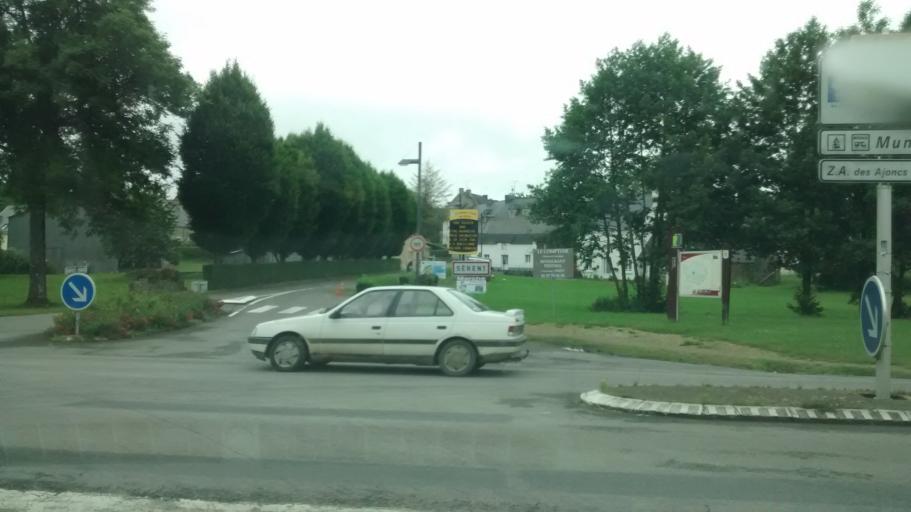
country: FR
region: Brittany
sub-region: Departement du Morbihan
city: Serent
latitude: 47.8221
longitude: -2.5025
